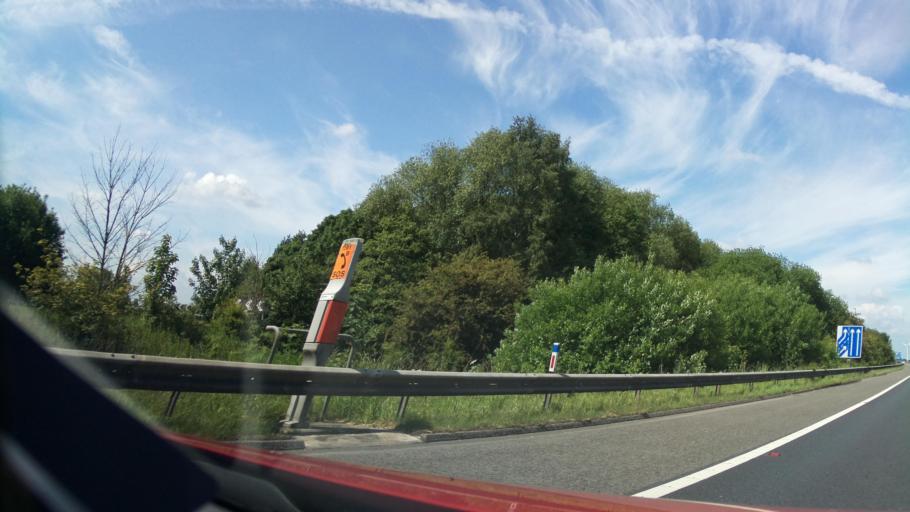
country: GB
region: England
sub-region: North Lincolnshire
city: Gunness
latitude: 53.5572
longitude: -0.7142
